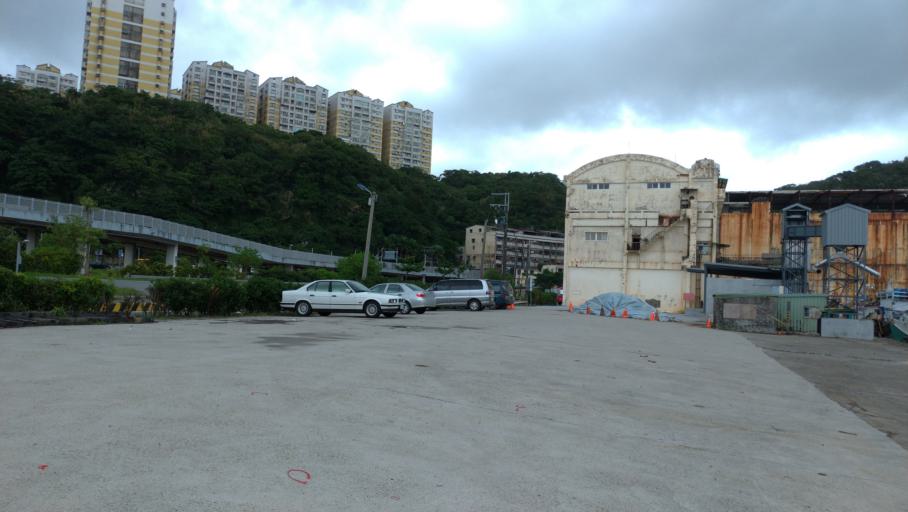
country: TW
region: Taiwan
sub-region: Keelung
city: Keelung
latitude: 25.1410
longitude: 121.7947
